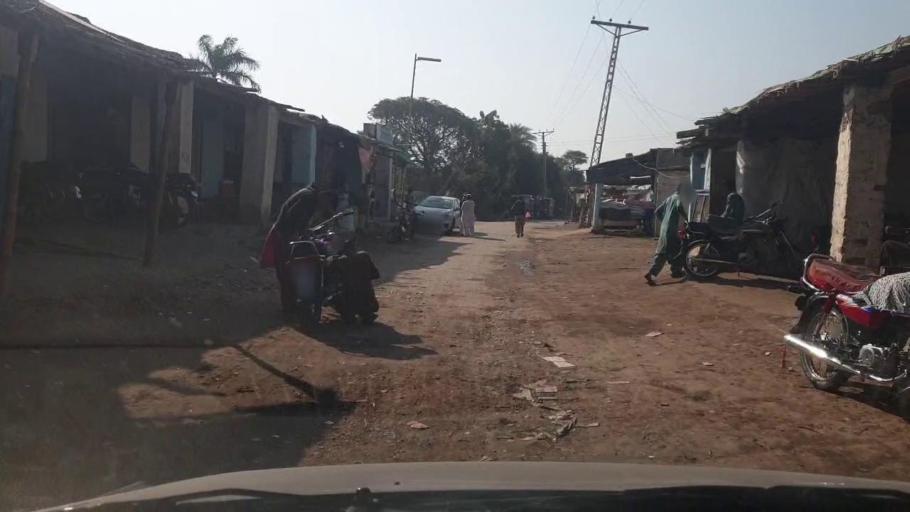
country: PK
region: Sindh
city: Mirwah Gorchani
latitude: 25.3127
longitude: 69.1522
